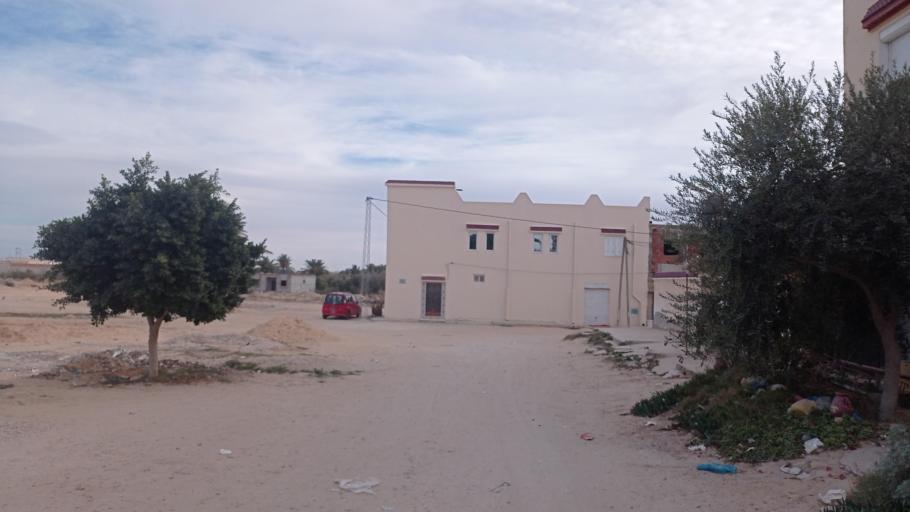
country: TN
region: Qabis
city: Gabes
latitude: 33.8375
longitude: 10.1159
